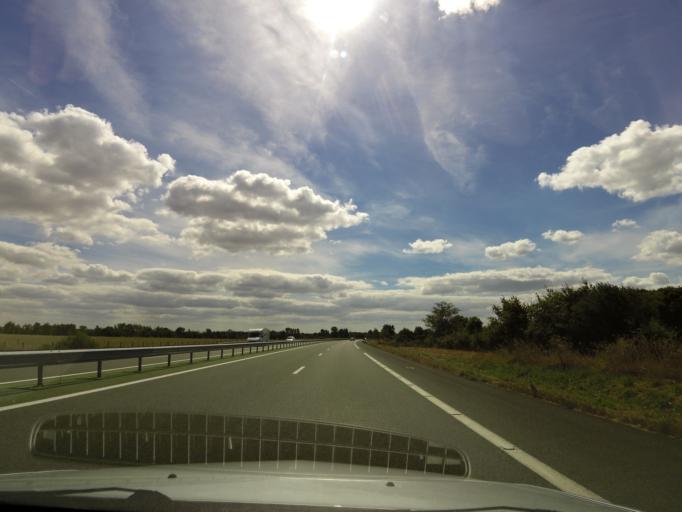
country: FR
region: Pays de la Loire
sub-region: Departement de la Vendee
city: La Ferriere
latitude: 46.7031
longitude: -1.2913
